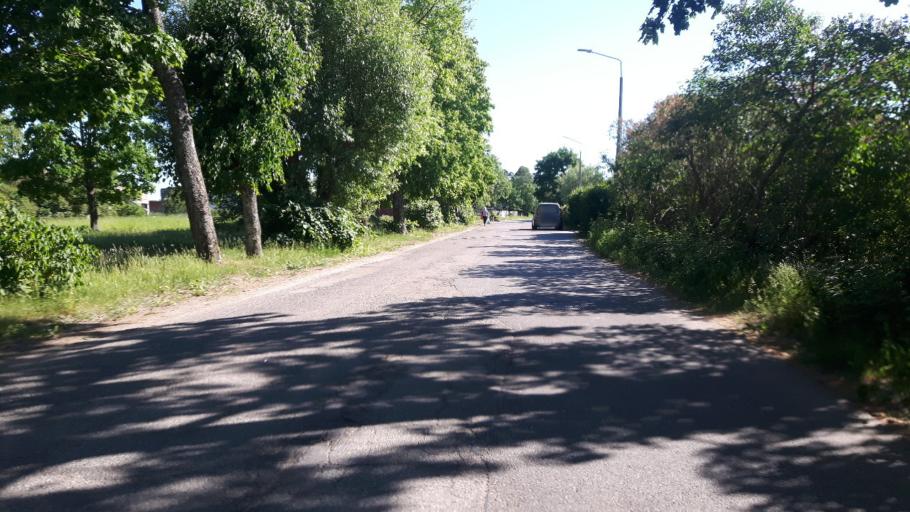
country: LV
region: Salacgrivas
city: Salacgriva
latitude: 57.7503
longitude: 24.3554
